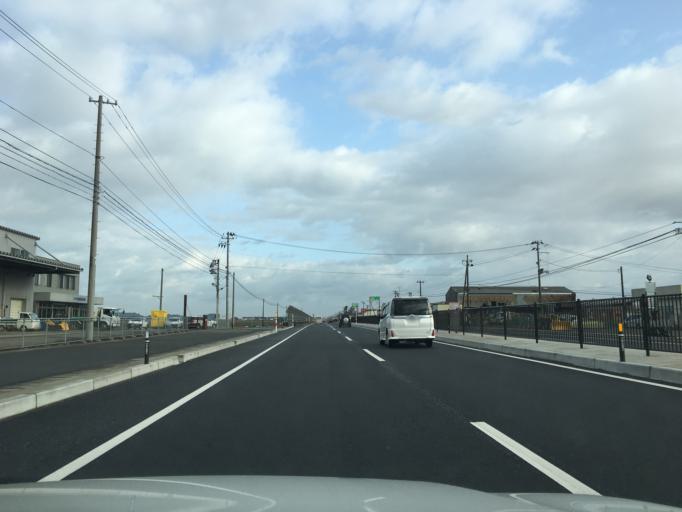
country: JP
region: Yamagata
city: Sakata
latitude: 38.8528
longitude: 139.8472
